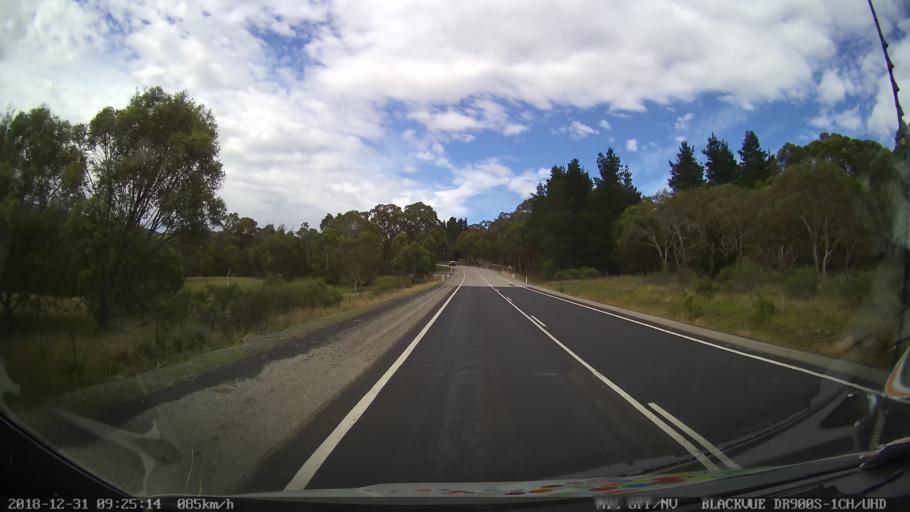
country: AU
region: New South Wales
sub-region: Snowy River
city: Jindabyne
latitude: -36.4418
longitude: 148.5098
